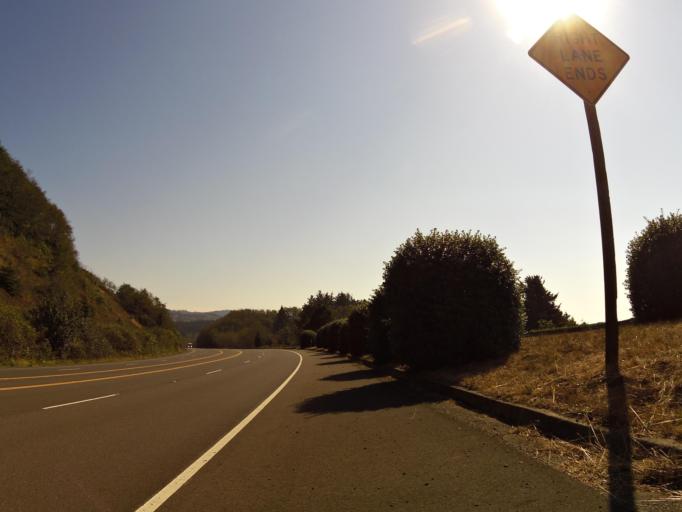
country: US
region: Oregon
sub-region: Tillamook County
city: Pacific City
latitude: 45.1425
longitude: -123.9694
